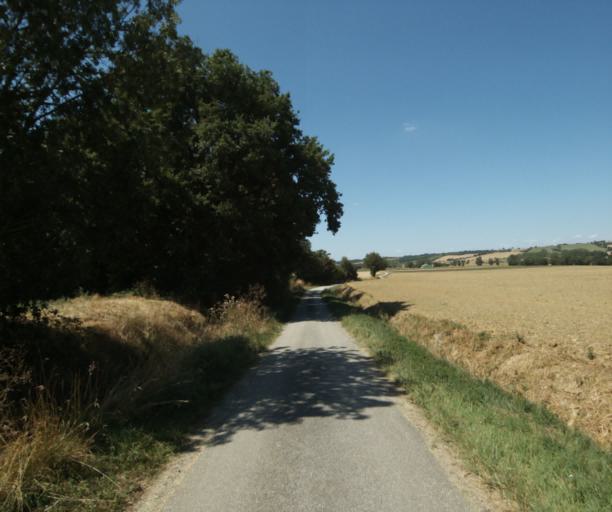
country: FR
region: Midi-Pyrenees
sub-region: Departement de la Haute-Garonne
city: Saint-Felix-Lauragais
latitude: 43.4771
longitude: 1.8787
